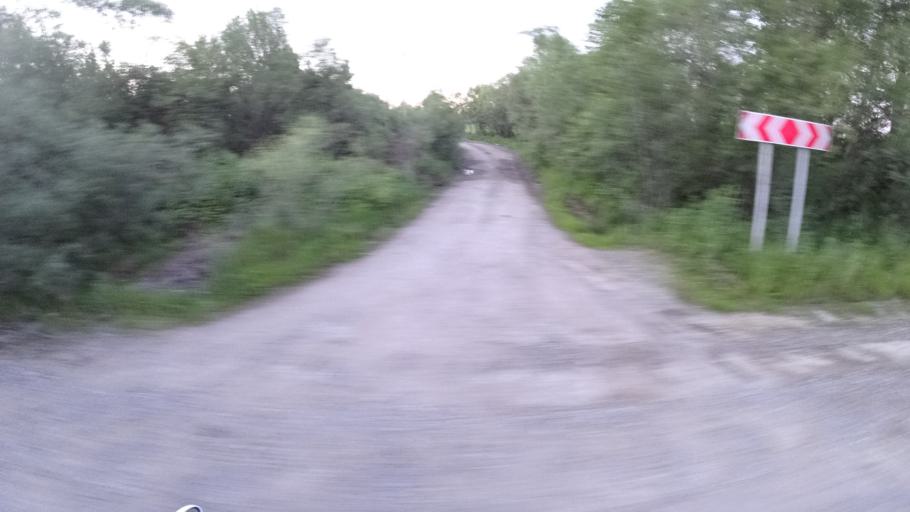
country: RU
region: Khabarovsk Krai
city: Khor
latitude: 47.8435
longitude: 134.9515
